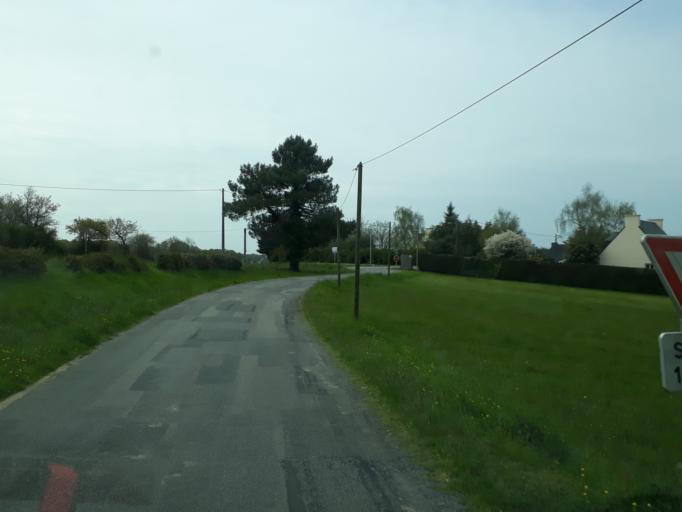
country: FR
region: Brittany
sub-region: Departement du Morbihan
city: Theix
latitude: 47.5892
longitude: -2.6866
